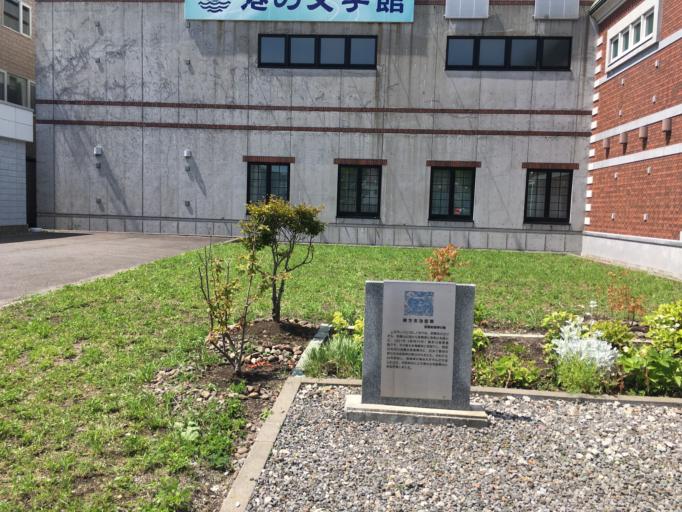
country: JP
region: Hokkaido
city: Muroran
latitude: 42.3188
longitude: 140.9732
